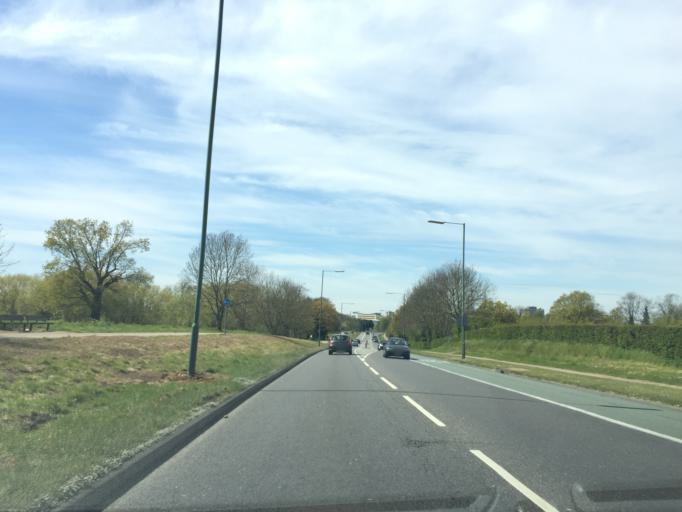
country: GB
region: England
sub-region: Essex
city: Harlow
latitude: 51.7652
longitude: 0.1115
